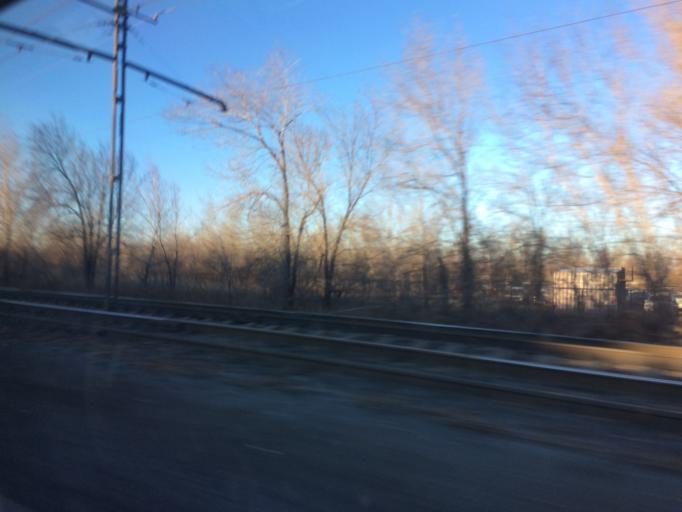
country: RU
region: Chelyabinsk
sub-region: Gorod Magnitogorsk
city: Magnitogorsk
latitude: 53.4094
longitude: 59.0315
